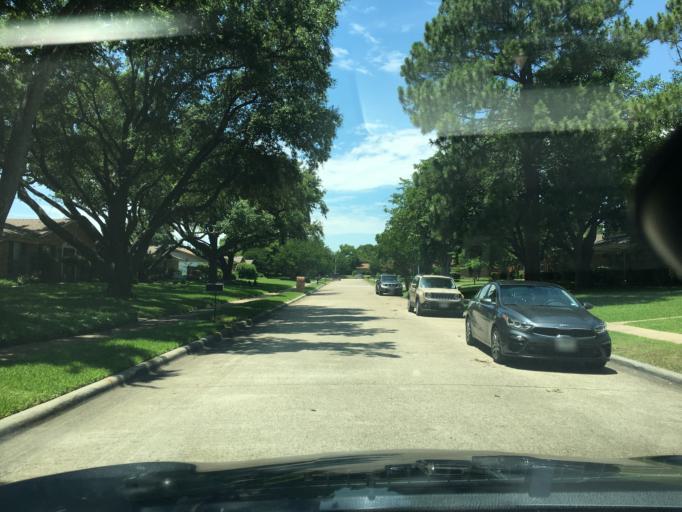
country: US
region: Texas
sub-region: Dallas County
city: Richardson
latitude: 32.9327
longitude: -96.6943
